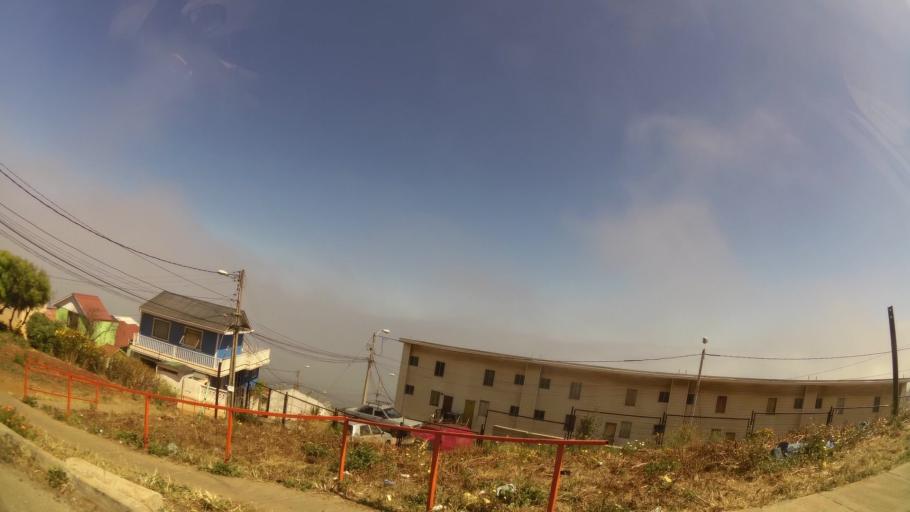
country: CL
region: Valparaiso
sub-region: Provincia de Valparaiso
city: Valparaiso
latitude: -33.0405
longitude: -71.6559
